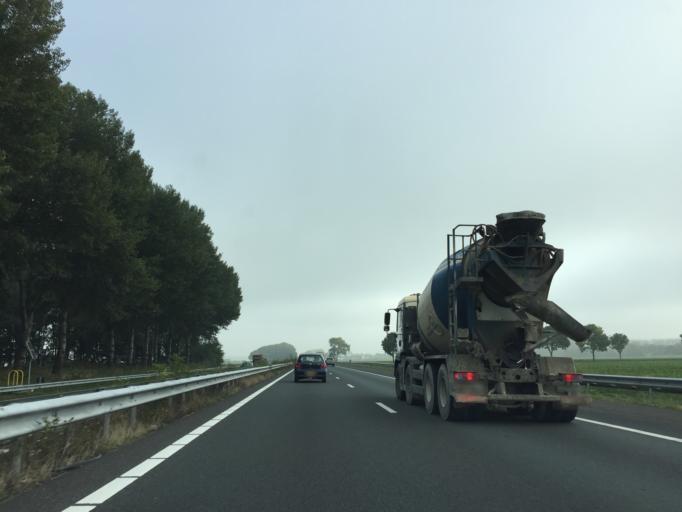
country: NL
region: North Brabant
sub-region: Gemeente Waalwijk
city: Waspik
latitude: 51.6943
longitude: 4.9659
